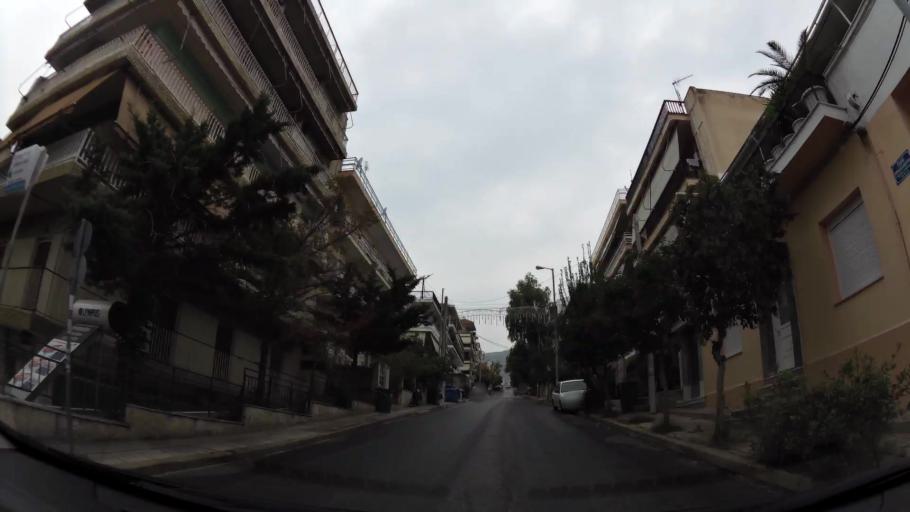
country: GR
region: Attica
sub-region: Nomos Piraios
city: Korydallos
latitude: 37.9851
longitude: 23.6467
